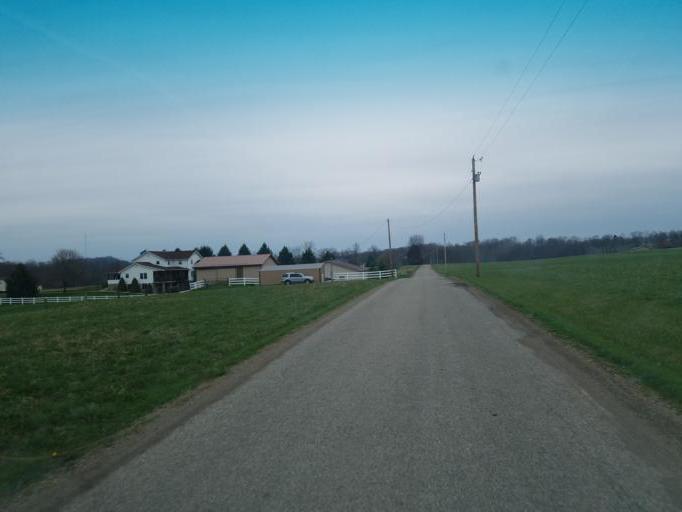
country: US
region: Ohio
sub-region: Holmes County
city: Millersburg
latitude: 40.6548
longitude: -81.9144
